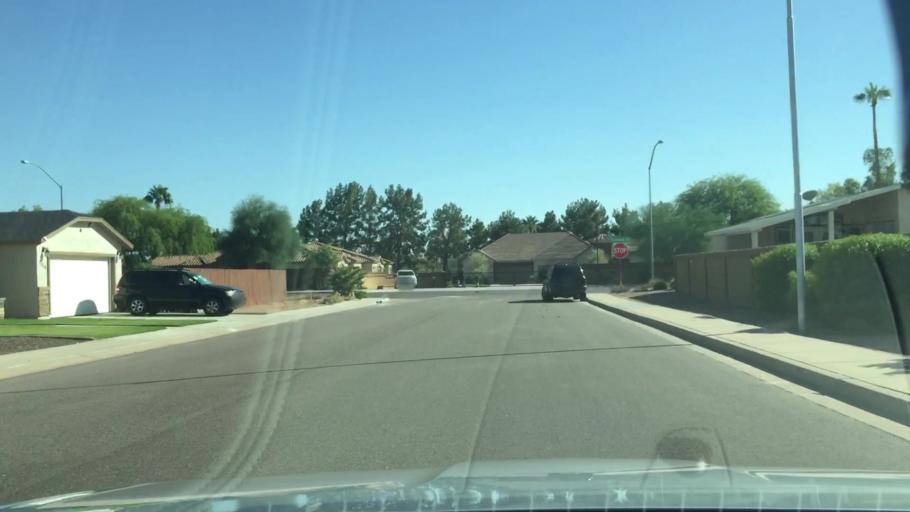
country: US
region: Arizona
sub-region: Pinal County
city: Apache Junction
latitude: 33.4085
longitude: -111.6605
